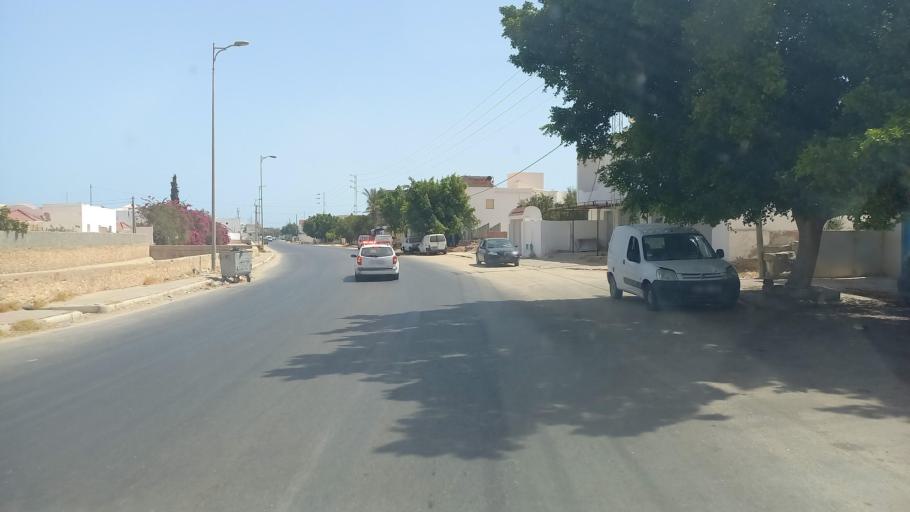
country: TN
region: Madanin
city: Zarzis
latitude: 33.4927
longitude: 11.0763
